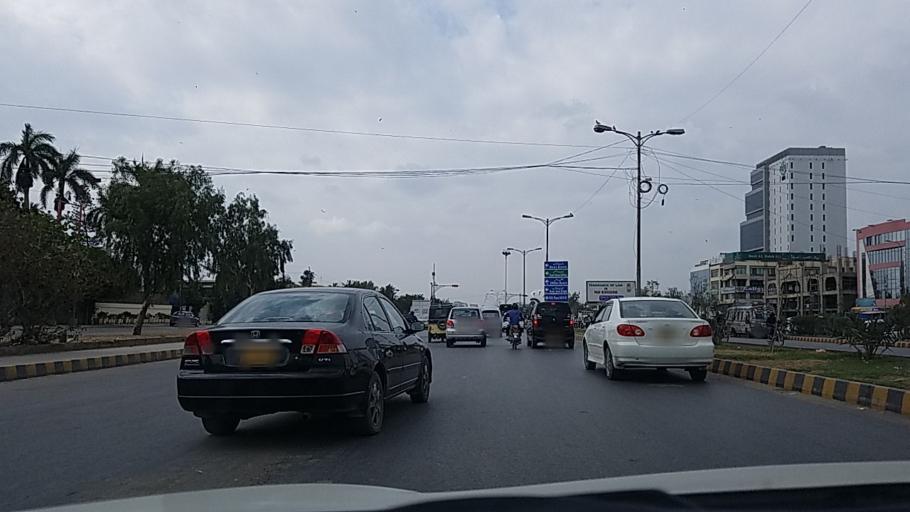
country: PK
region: Sindh
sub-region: Karachi District
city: Karachi
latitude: 24.8362
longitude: 67.0691
